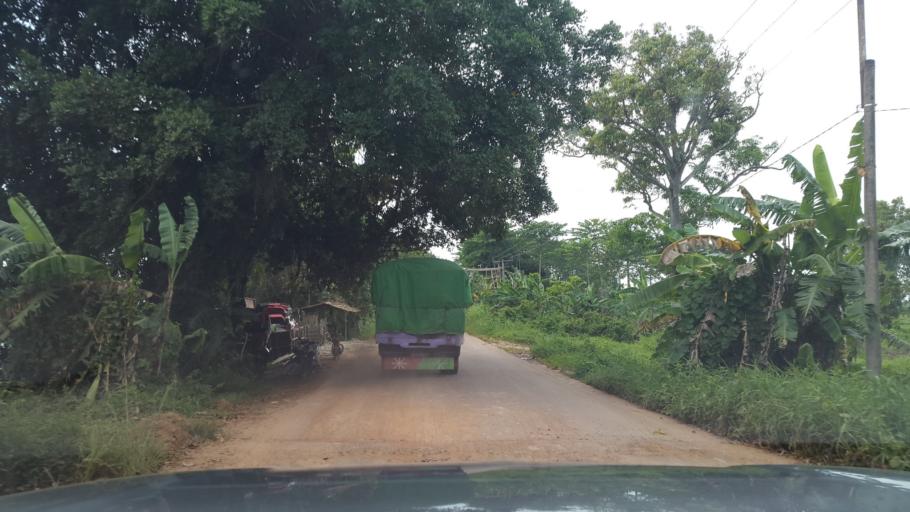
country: ID
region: South Sumatra
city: Tanjungraja
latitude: -3.1782
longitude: 104.8585
